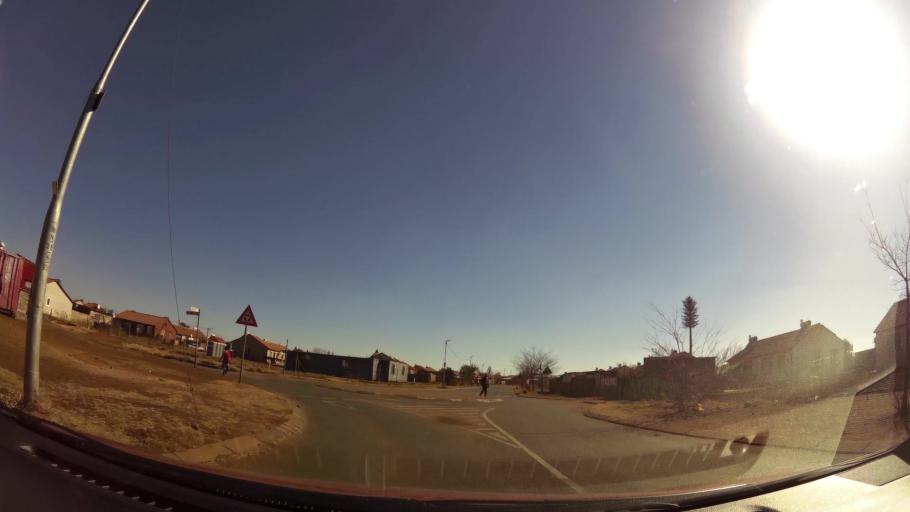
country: ZA
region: Gauteng
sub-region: City of Johannesburg Metropolitan Municipality
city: Soweto
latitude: -26.2412
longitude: 27.8001
